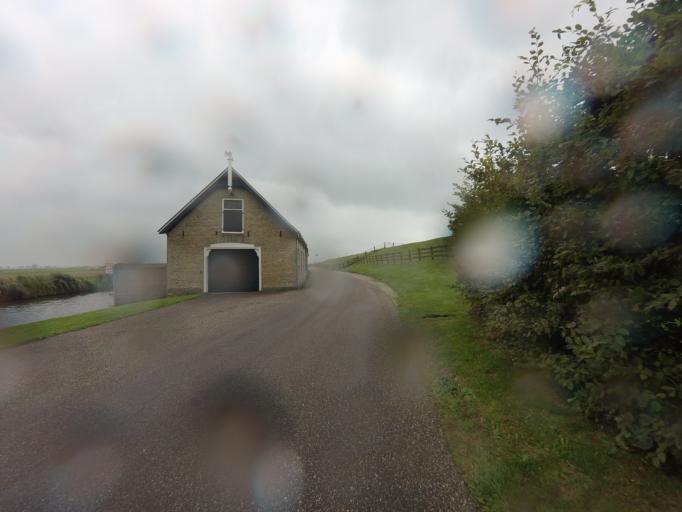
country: NL
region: Friesland
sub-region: Sudwest Fryslan
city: Koudum
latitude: 52.9247
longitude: 5.4103
